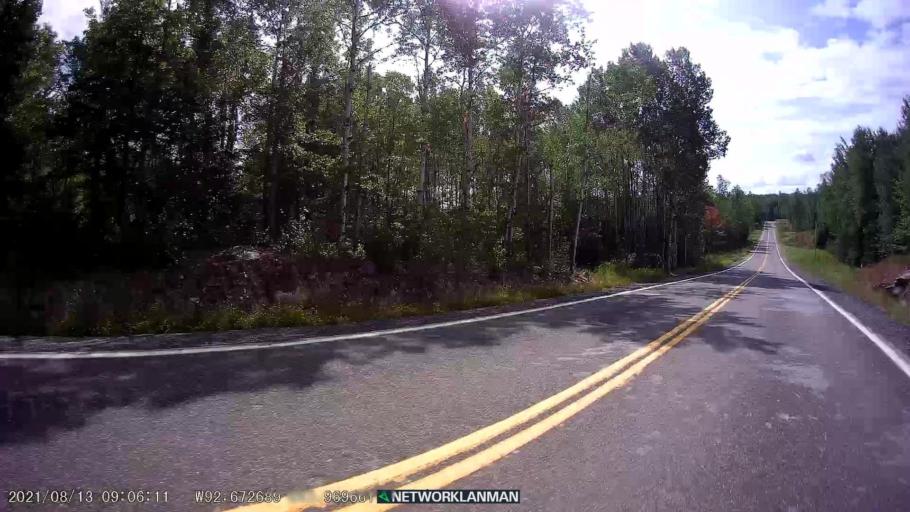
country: US
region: Minnesota
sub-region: Saint Louis County
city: Mountain Iron
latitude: 47.9691
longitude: -92.6724
